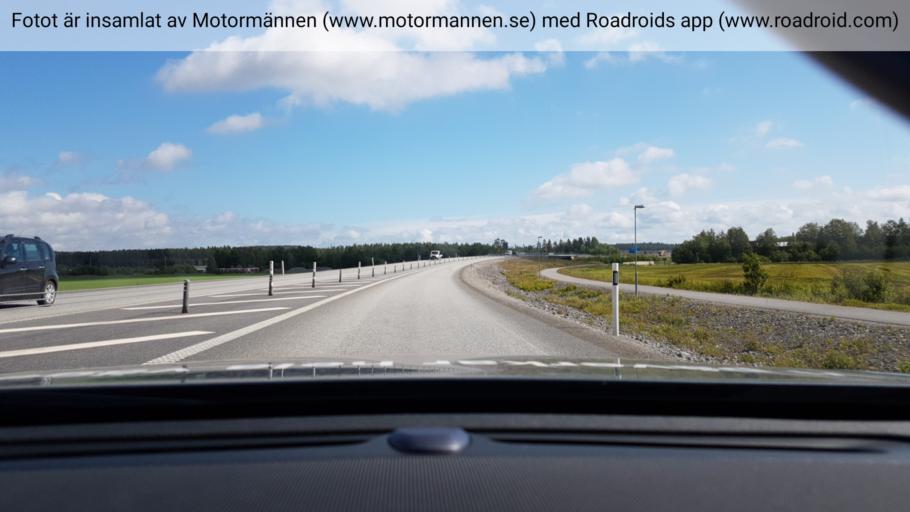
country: SE
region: Vaesterbotten
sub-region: Umea Kommun
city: Roback
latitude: 63.8537
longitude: 20.1952
